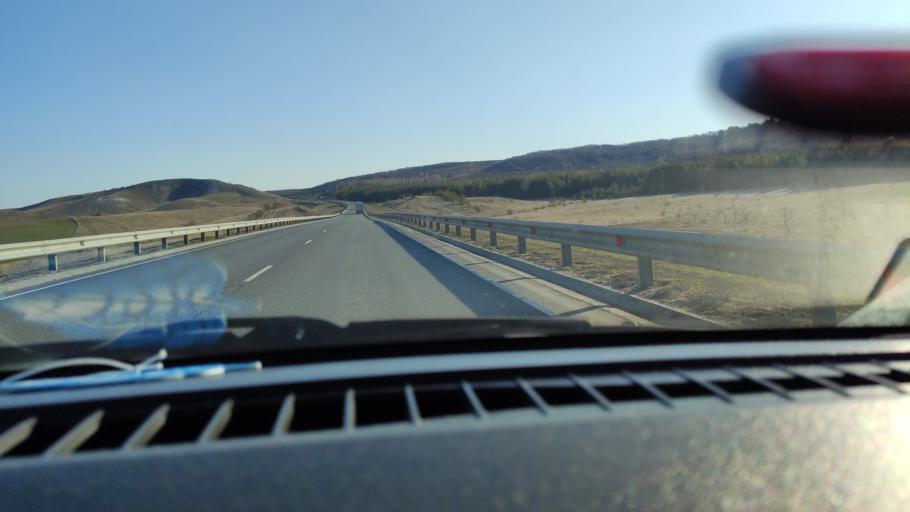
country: RU
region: Saratov
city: Alekseyevka
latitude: 52.3648
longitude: 47.9601
